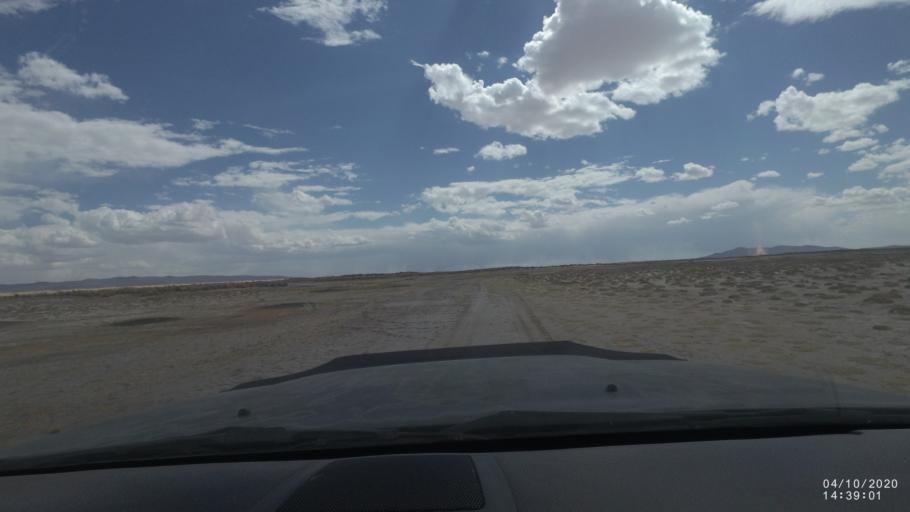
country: BO
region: Oruro
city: Poopo
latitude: -18.6784
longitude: -67.4834
